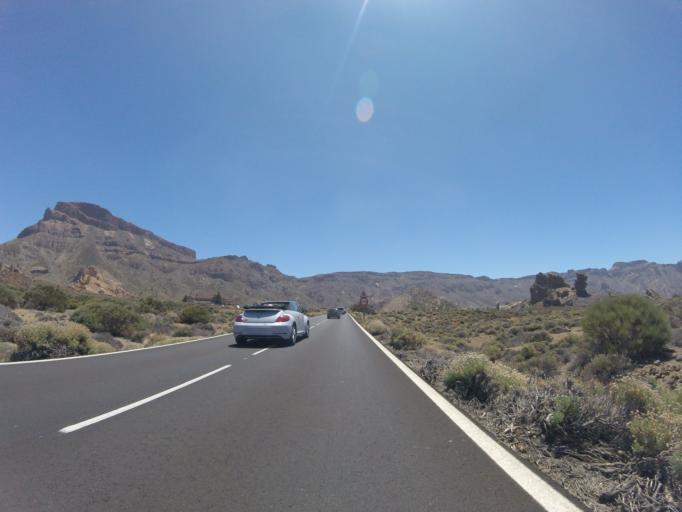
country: ES
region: Canary Islands
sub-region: Provincia de Santa Cruz de Tenerife
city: Vilaflor
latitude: 28.2275
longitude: -16.6290
